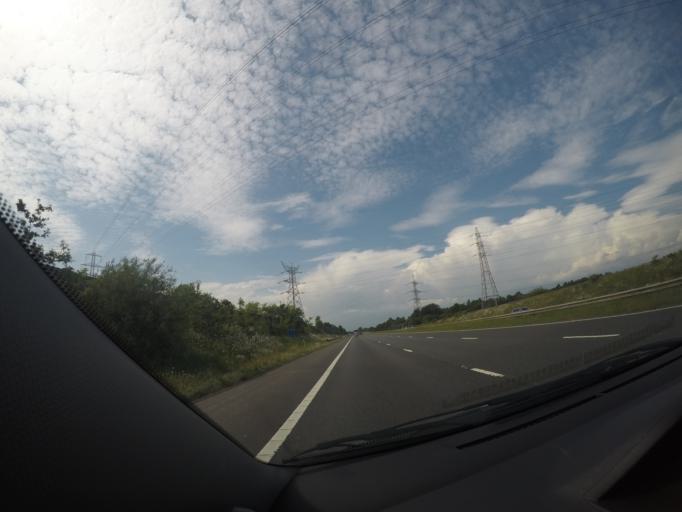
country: GB
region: England
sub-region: Cumbria
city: Carlisle
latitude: 54.9414
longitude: -2.9677
